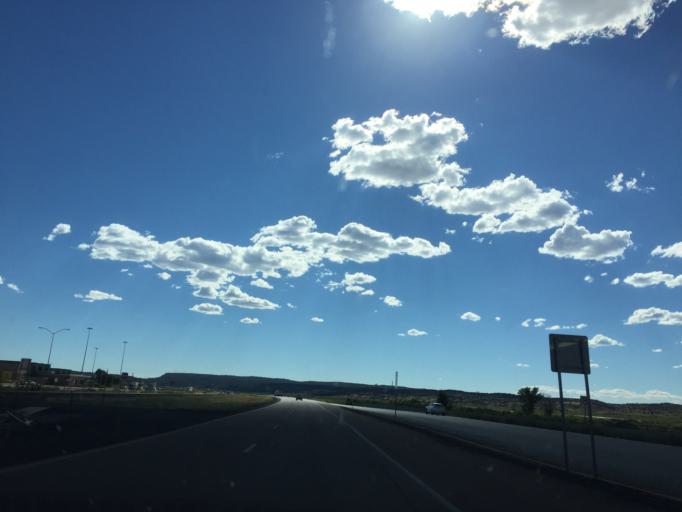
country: US
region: New Mexico
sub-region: McKinley County
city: Gallup
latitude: 35.4875
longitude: -108.8986
